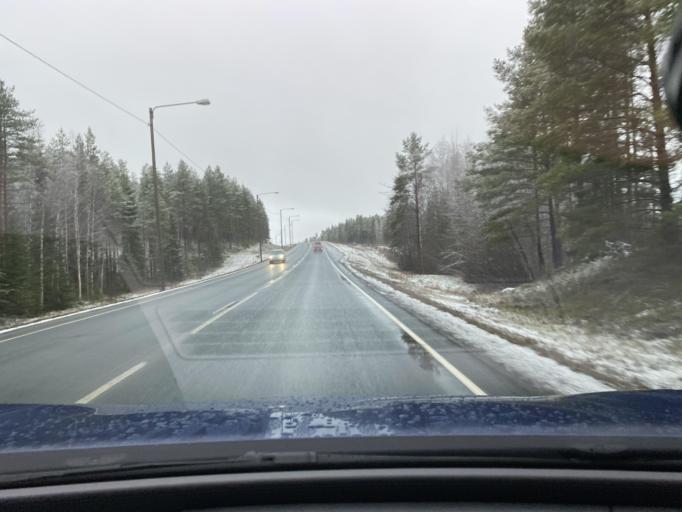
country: FI
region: Northern Ostrobothnia
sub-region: Oulu
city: Kiiminki
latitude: 65.1244
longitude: 25.7603
